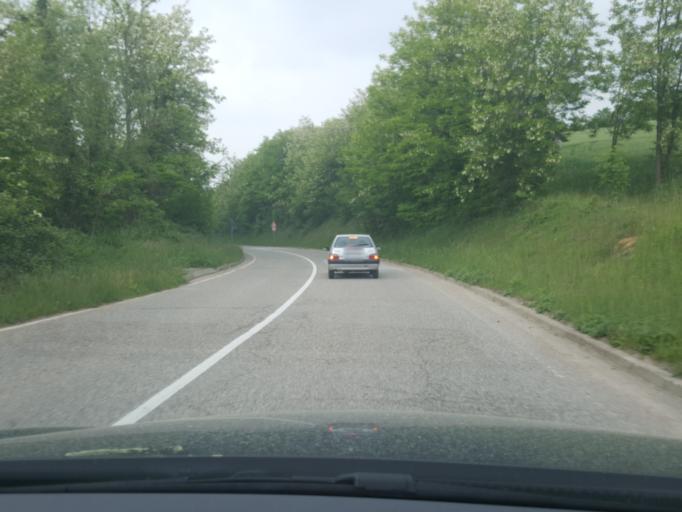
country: RS
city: Kamenica
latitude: 44.2471
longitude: 19.7435
